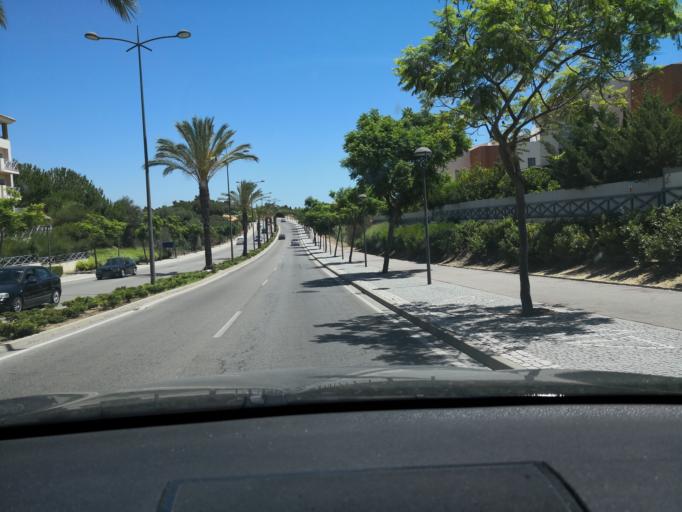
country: PT
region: Faro
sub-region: Albufeira
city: Albufeira
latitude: 37.0965
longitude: -8.2222
